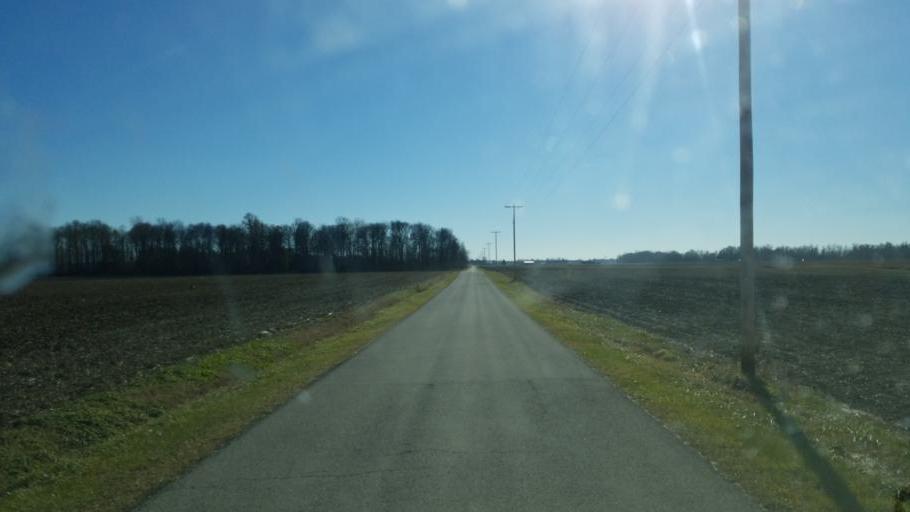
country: US
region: Ohio
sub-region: Crawford County
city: Galion
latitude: 40.7813
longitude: -82.8385
